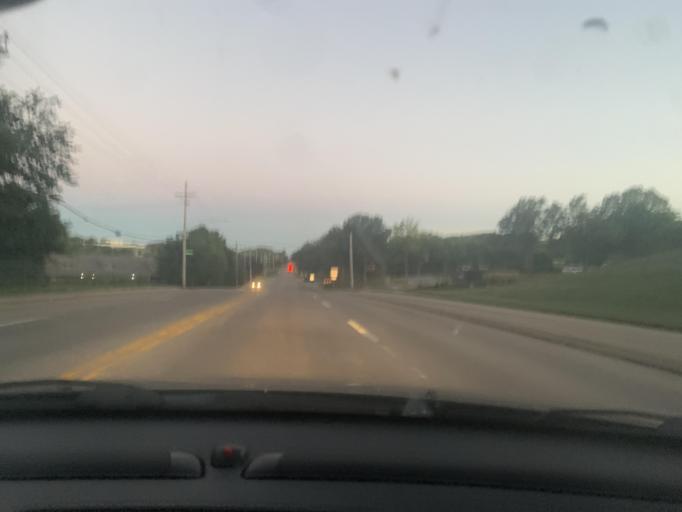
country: US
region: Nebraska
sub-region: Douglas County
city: Ralston
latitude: 41.2712
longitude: -96.0622
